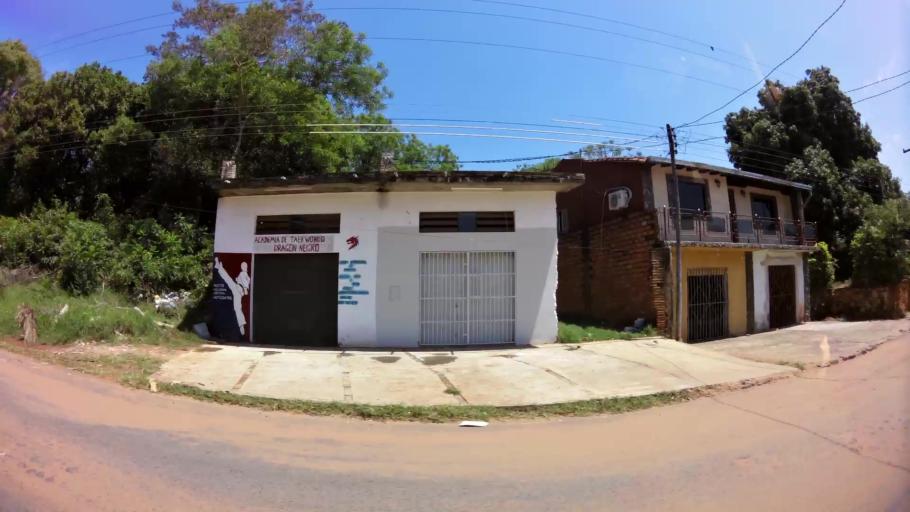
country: PY
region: Central
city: Nemby
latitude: -25.4061
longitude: -57.5266
